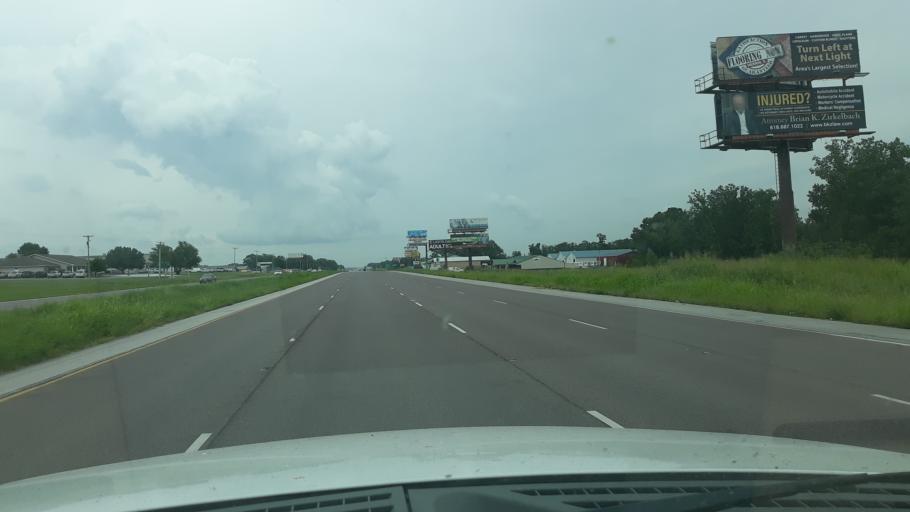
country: US
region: Illinois
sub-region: Williamson County
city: Crainville
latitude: 37.7449
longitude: -89.0527
